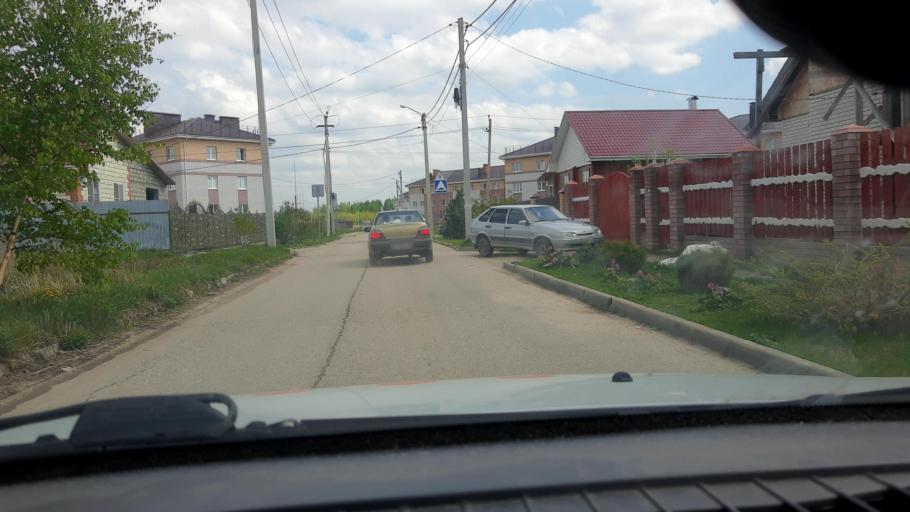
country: RU
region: Nizjnij Novgorod
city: Bor
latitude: 56.3910
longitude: 44.0555
